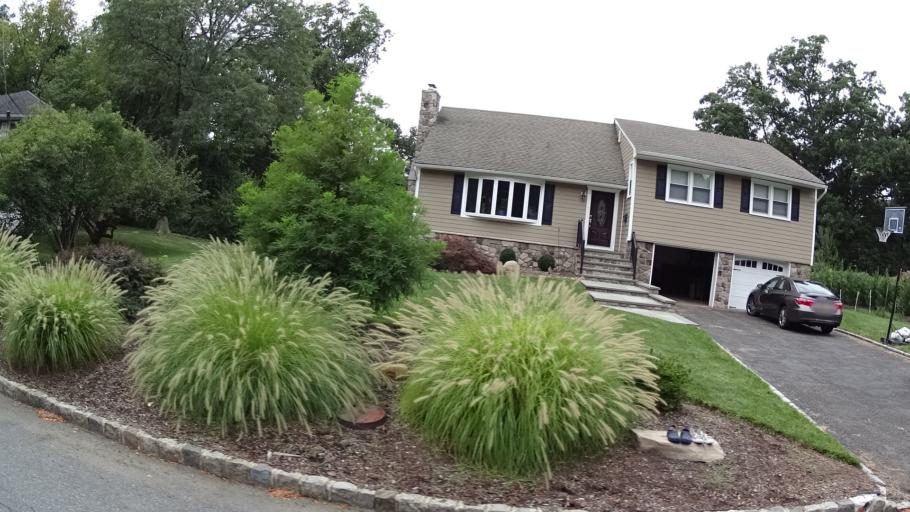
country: US
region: New Jersey
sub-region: Union County
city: New Providence
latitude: 40.7132
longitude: -74.3945
